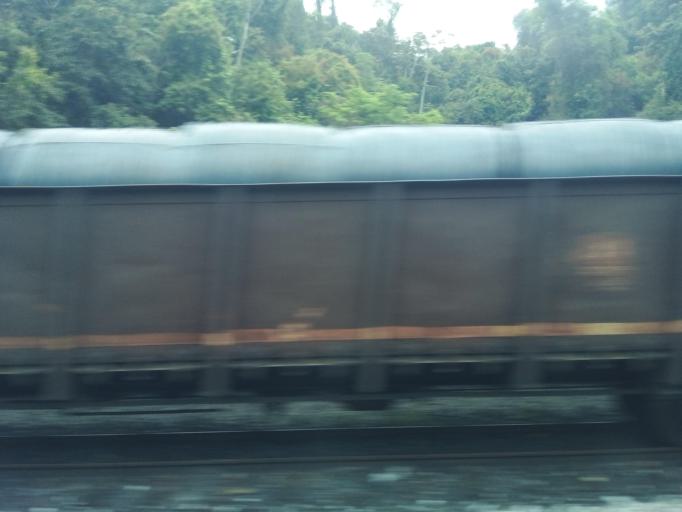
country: BR
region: Minas Gerais
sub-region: Joao Monlevade
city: Joao Monlevade
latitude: -19.8453
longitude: -43.1245
